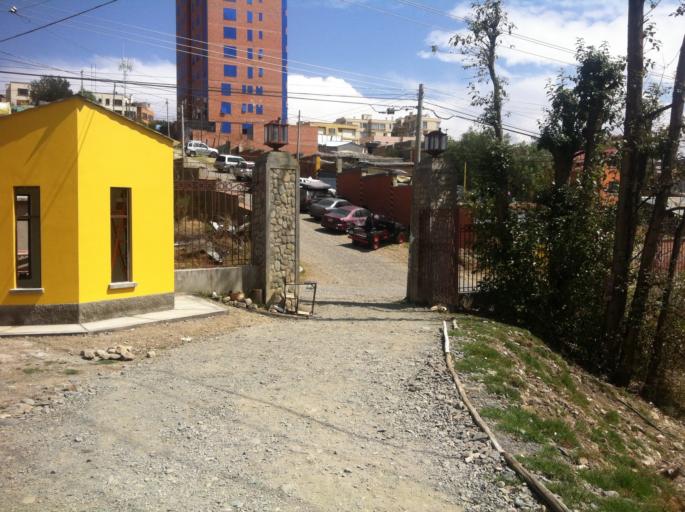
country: BO
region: La Paz
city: La Paz
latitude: -16.5393
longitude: -68.0660
